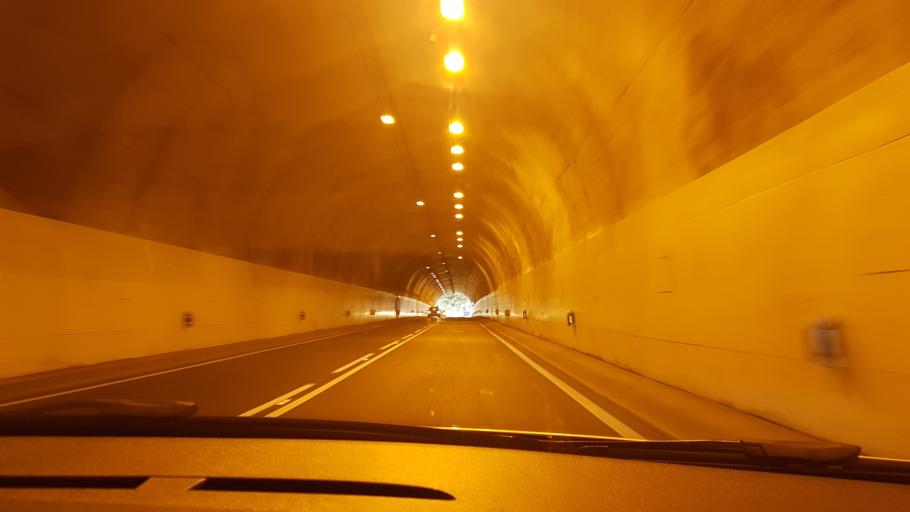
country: PT
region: Madeira
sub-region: Santana
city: Santana
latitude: 32.8095
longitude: -16.8777
